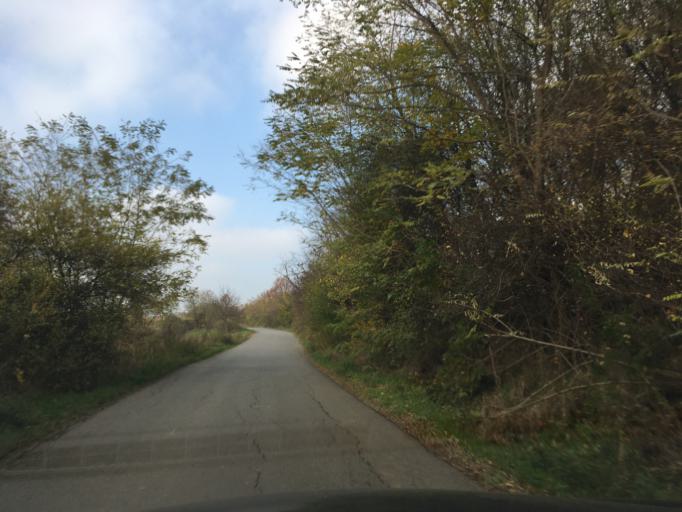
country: RS
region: Central Serbia
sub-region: Belgrade
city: Sopot
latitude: 44.4920
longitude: 20.5879
